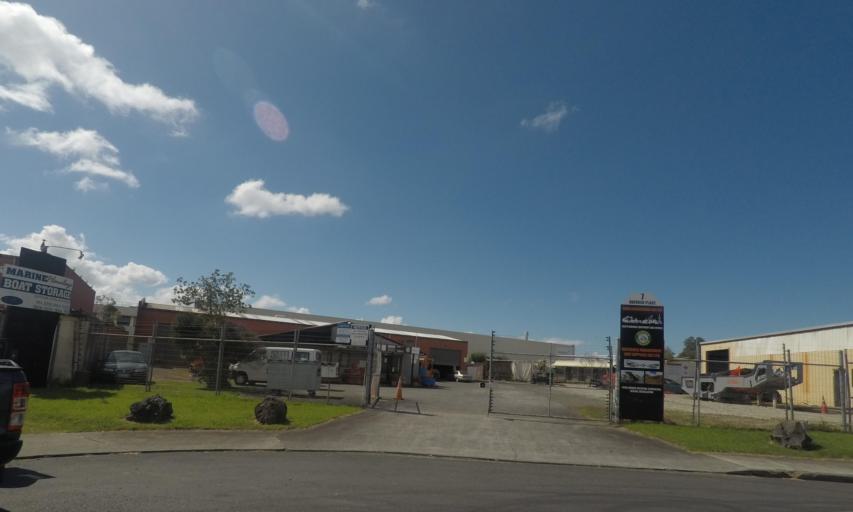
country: NZ
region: Auckland
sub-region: Auckland
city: Rosebank
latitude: -36.8859
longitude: 174.6642
